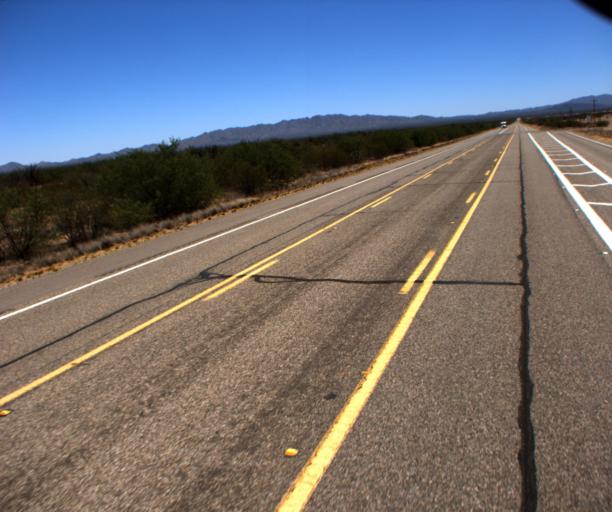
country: US
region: Arizona
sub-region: Pima County
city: Ajo
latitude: 32.1889
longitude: -112.4011
